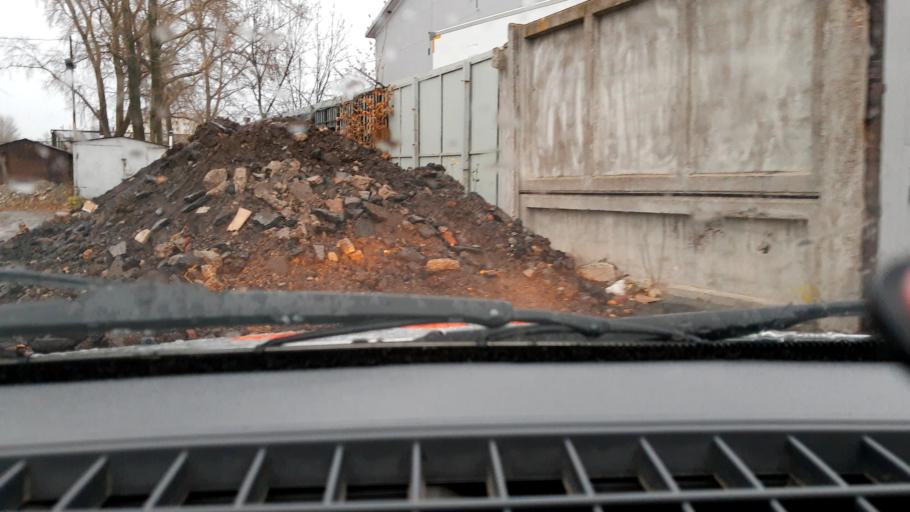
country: RU
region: Bashkortostan
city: Ufa
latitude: 54.8254
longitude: 56.1052
